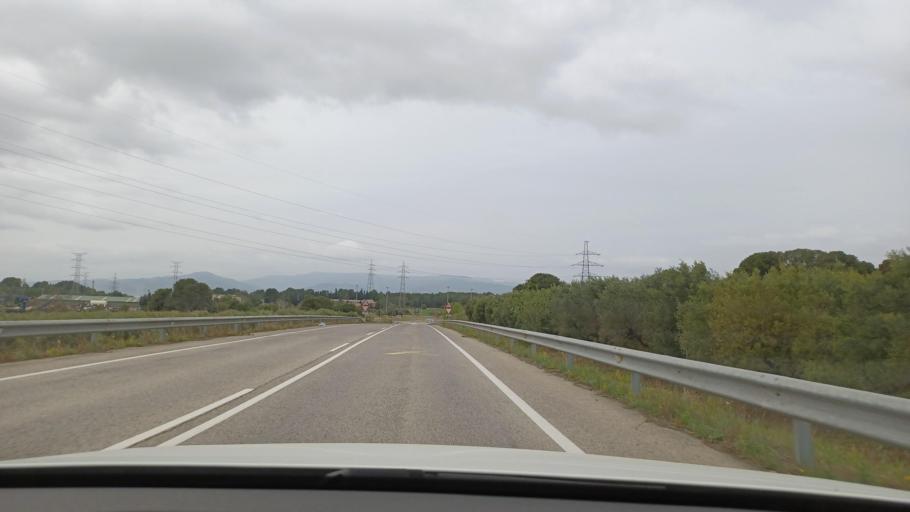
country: ES
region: Catalonia
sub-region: Provincia de Tarragona
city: La Secuita
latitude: 41.1998
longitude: 1.2480
